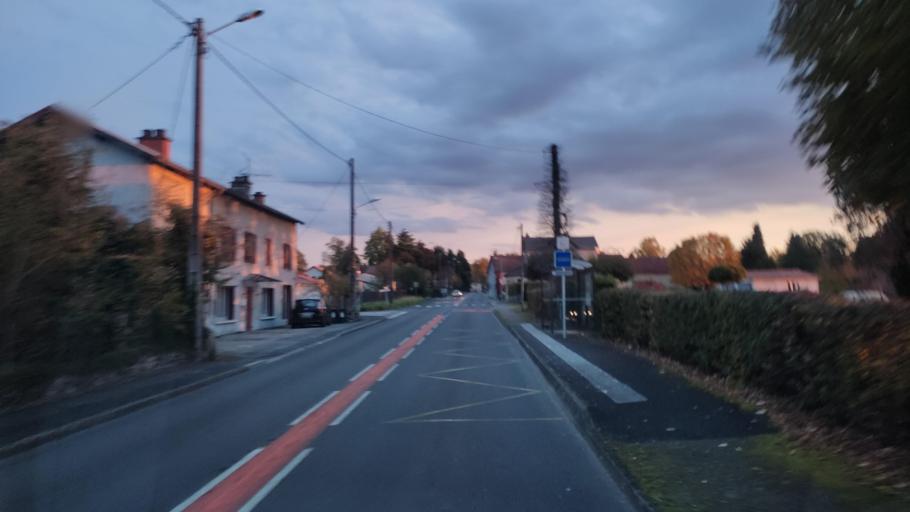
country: FR
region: Limousin
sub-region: Departement de la Haute-Vienne
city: Rilhac-Rancon
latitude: 45.9270
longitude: 1.3442
